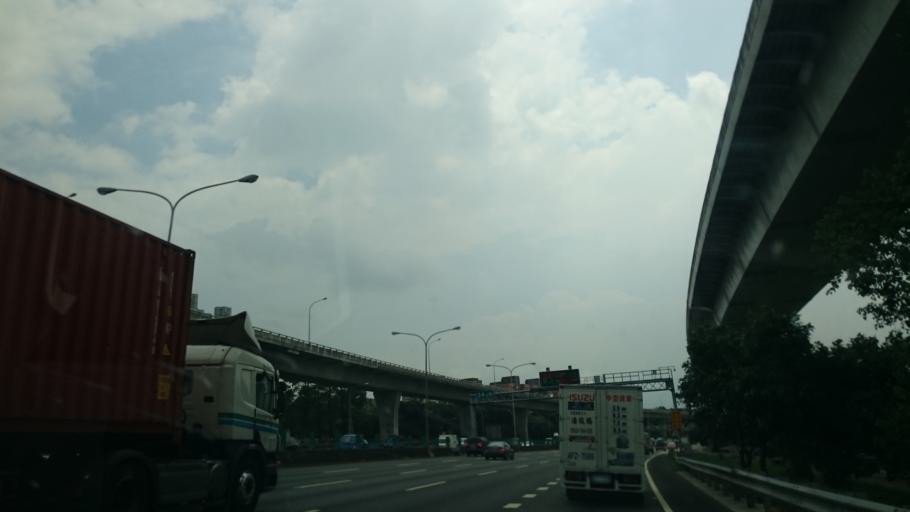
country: TW
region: Taipei
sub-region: Taipei
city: Banqiao
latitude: 25.0673
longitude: 121.4257
